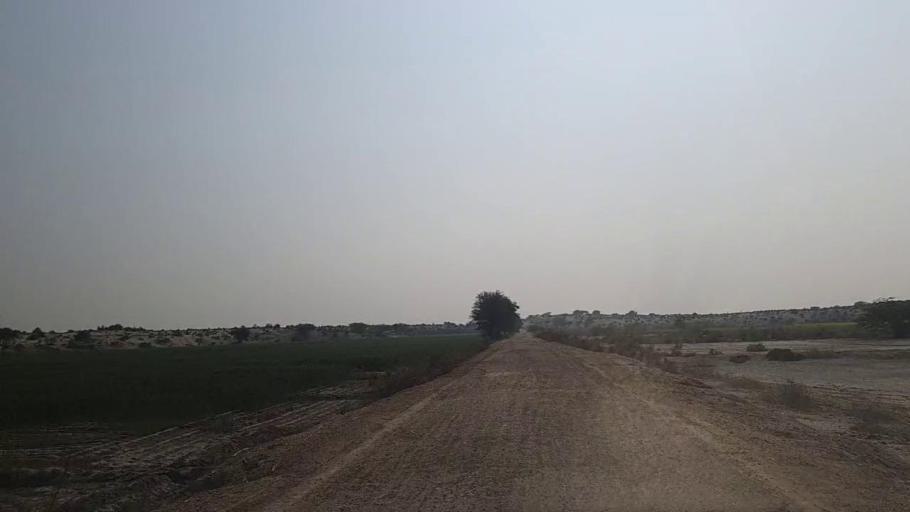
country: PK
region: Sindh
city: Jam Sahib
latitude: 26.4494
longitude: 68.5233
